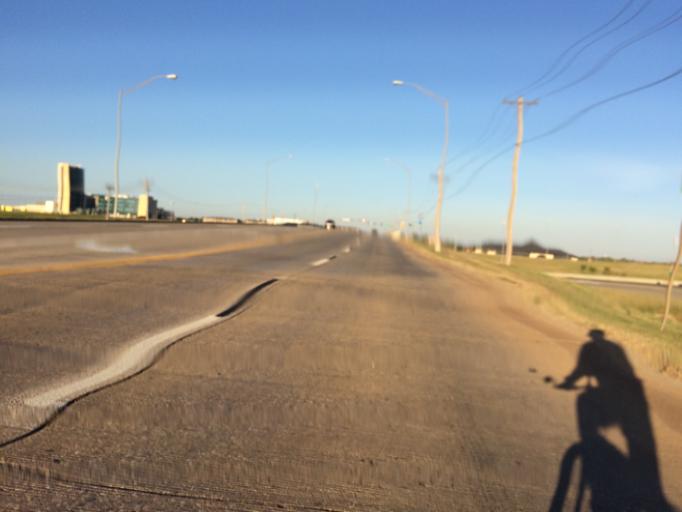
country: US
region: Oklahoma
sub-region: Cleveland County
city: Norman
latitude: 35.2621
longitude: -97.4839
